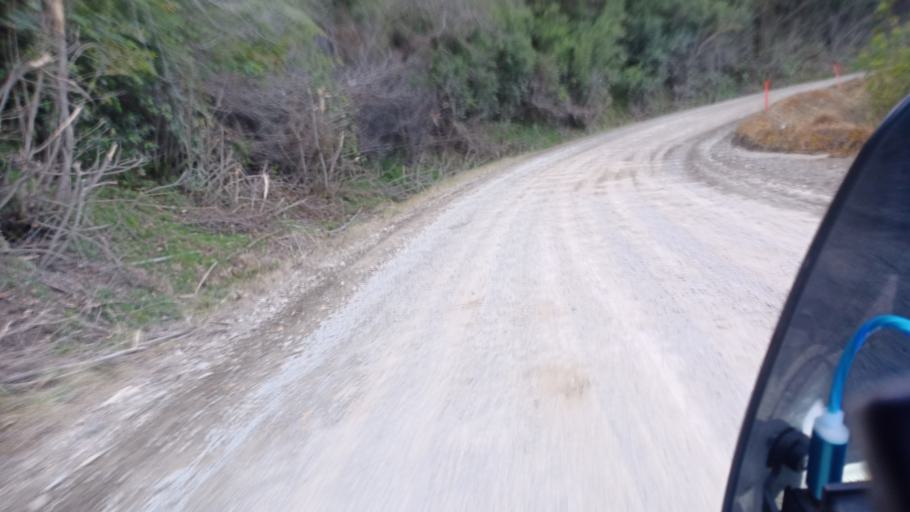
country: NZ
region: Gisborne
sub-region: Gisborne District
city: Gisborne
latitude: -38.1409
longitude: 178.1938
